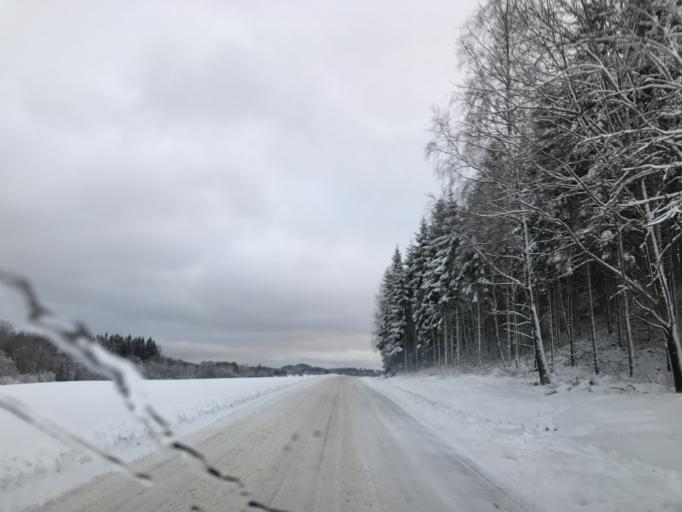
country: SE
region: Vaestra Goetaland
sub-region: Svenljunga Kommun
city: Svenljunga
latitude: 57.3234
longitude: 13.0266
